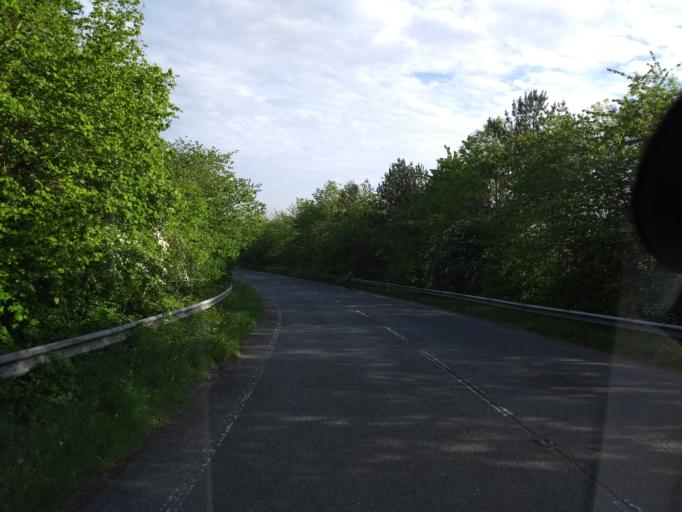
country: GB
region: England
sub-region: Devon
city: Axminster
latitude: 50.7672
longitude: -2.9780
